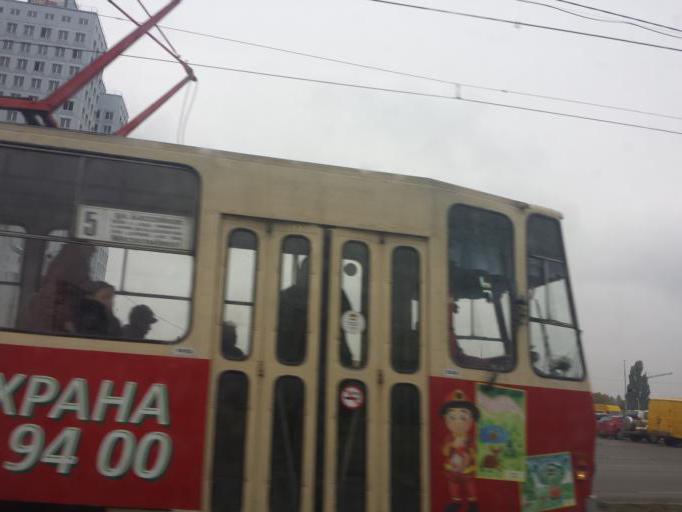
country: RU
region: Kaliningrad
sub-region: Gorod Kaliningrad
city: Kaliningrad
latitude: 54.7111
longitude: 20.5122
